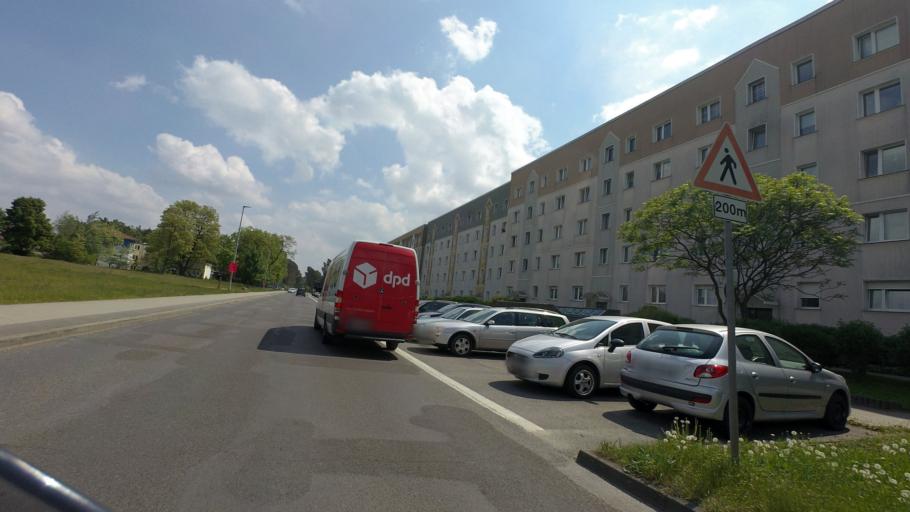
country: DE
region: Saxony
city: Weisswasser
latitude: 51.4969
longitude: 14.6432
